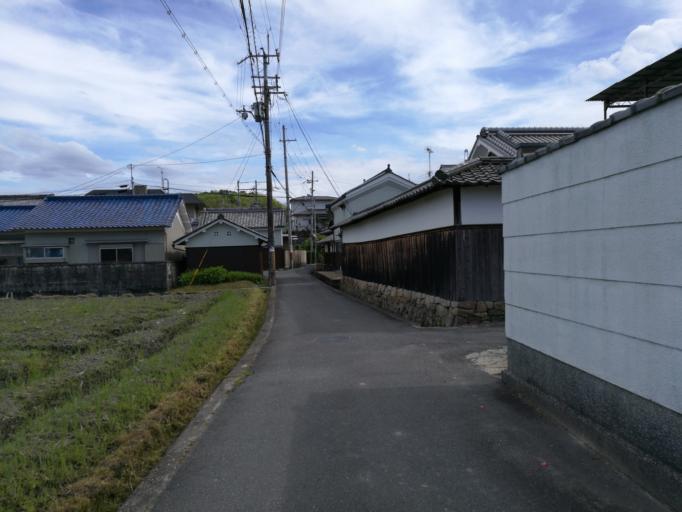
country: JP
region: Kyoto
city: Tanabe
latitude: 34.7585
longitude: 135.7817
